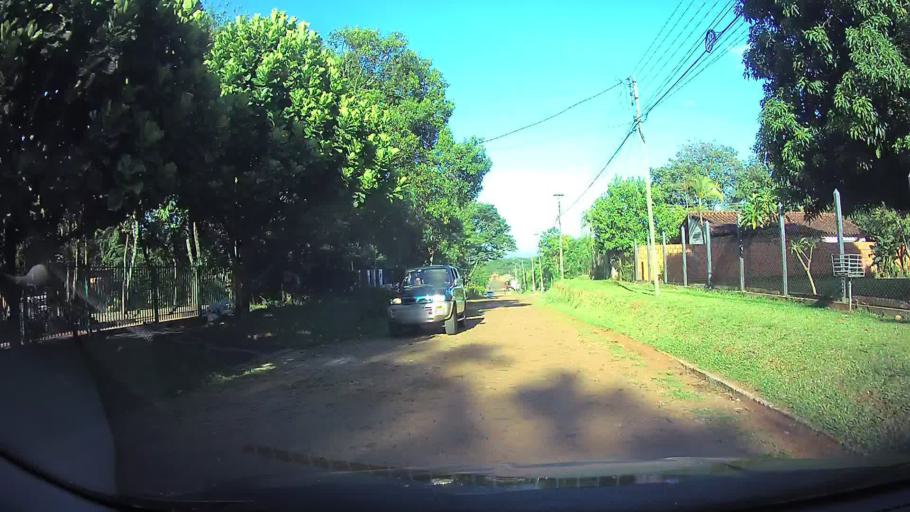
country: PY
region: Central
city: San Lorenzo
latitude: -25.2570
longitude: -57.4723
